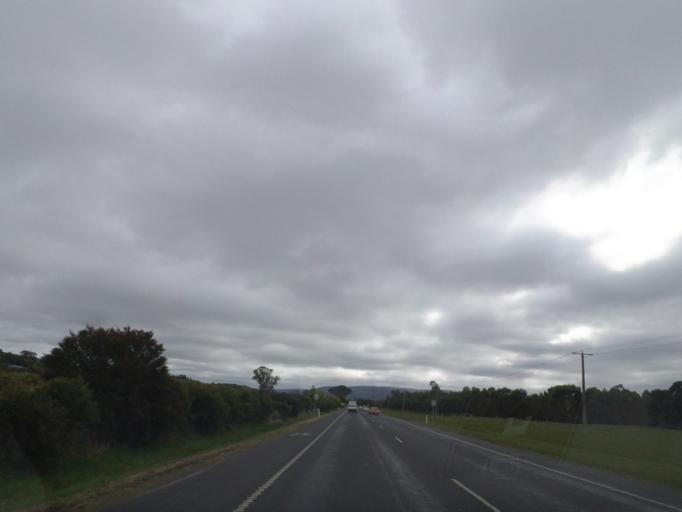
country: AU
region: Victoria
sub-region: Whittlesea
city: Whittlesea
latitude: -37.5334
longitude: 145.1117
